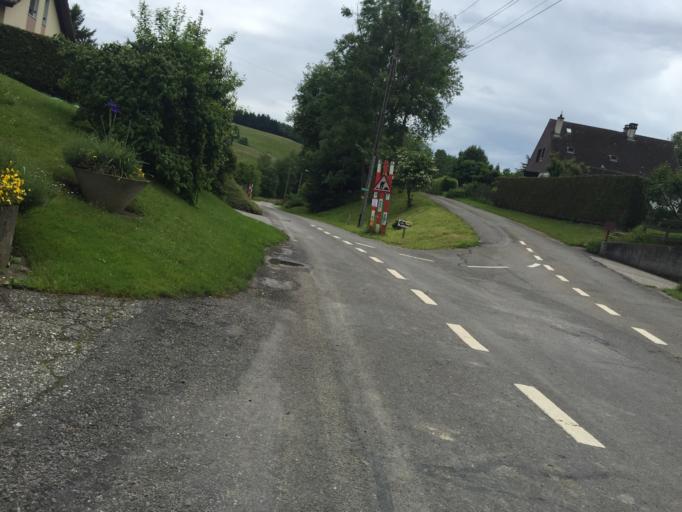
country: CH
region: Vaud
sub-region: Gros-de-Vaud District
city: Froideville
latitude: 46.5985
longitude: 6.6846
